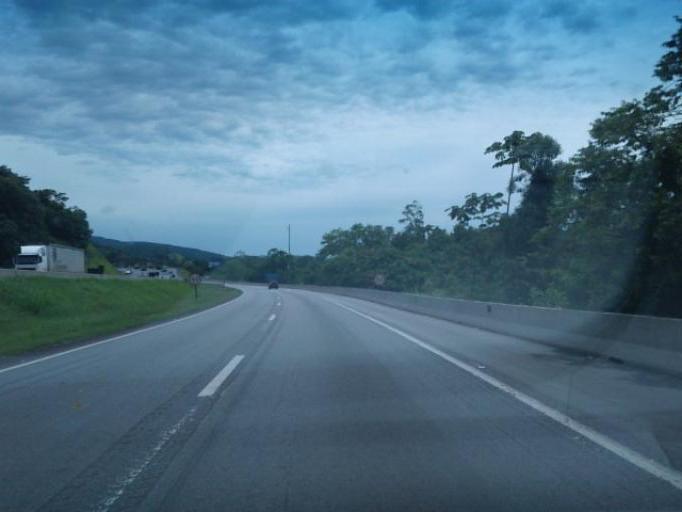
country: BR
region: Sao Paulo
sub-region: Miracatu
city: Miracatu
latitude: -24.1534
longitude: -47.3233
